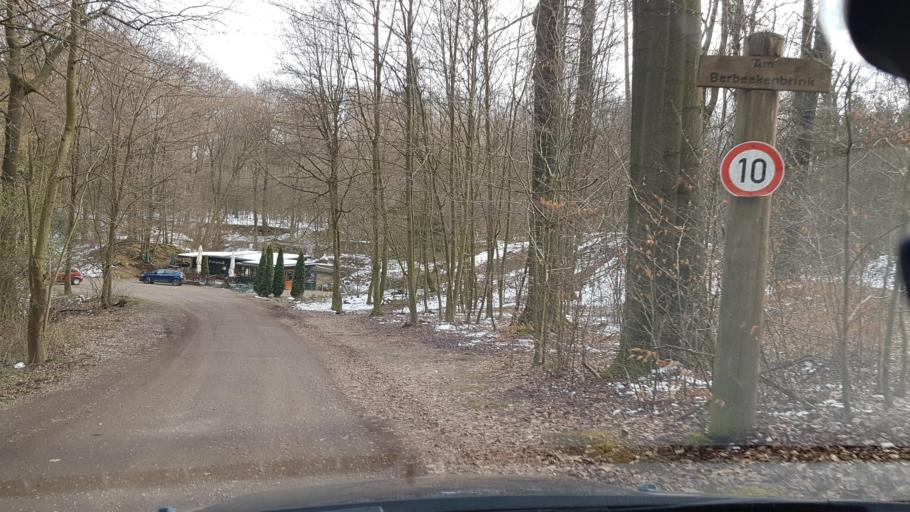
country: DE
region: Lower Saxony
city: Egestorf
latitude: 52.2844
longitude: 9.4845
